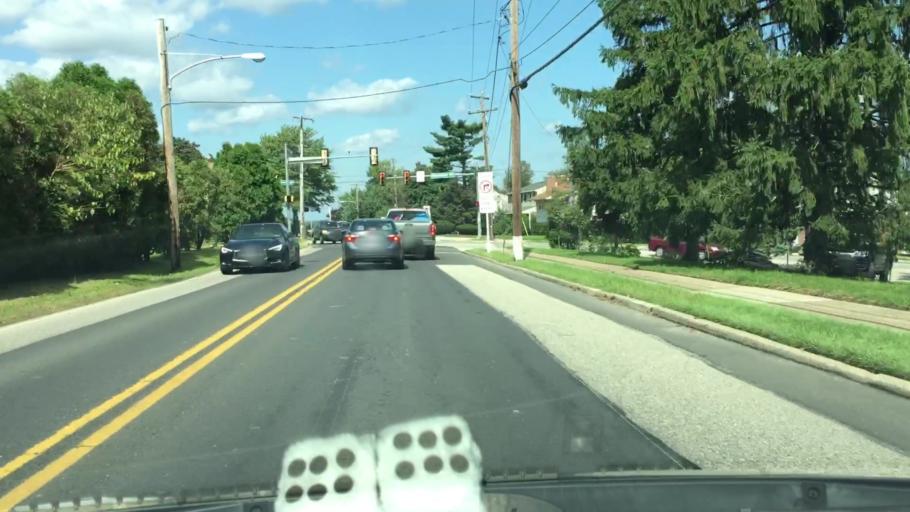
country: US
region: Pennsylvania
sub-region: Montgomery County
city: Norristown
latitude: 40.1202
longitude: -75.3070
